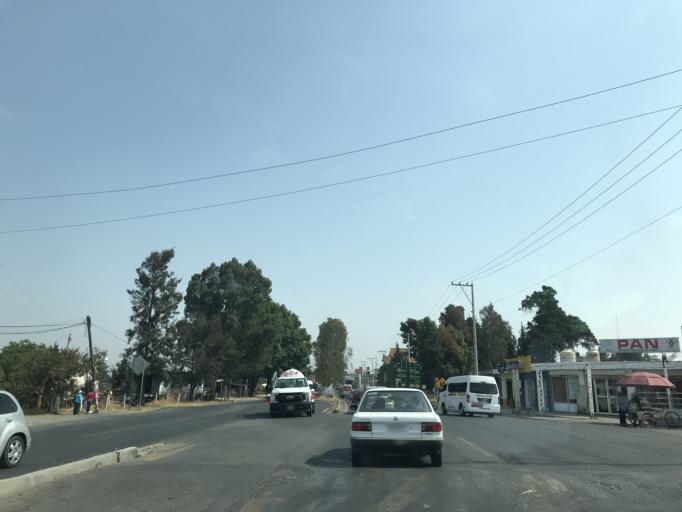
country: MX
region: Tlaxcala
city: La Magdalena Tlaltelulco
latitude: 19.2749
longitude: -98.1967
